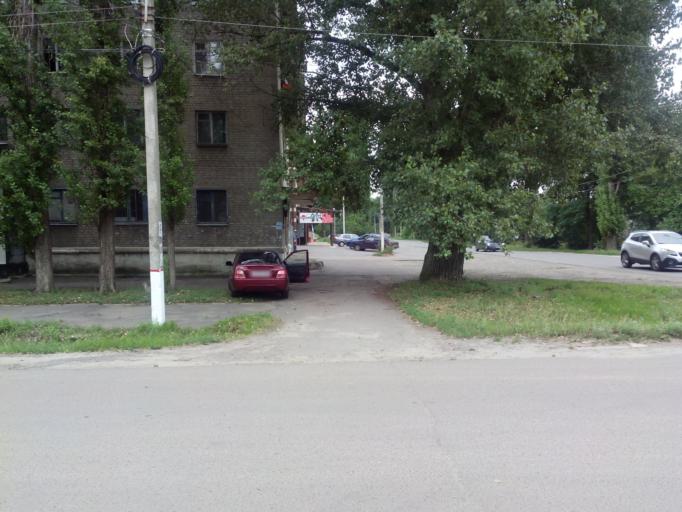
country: RU
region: Voronezj
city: Borisoglebsk
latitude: 51.3670
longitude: 42.0919
